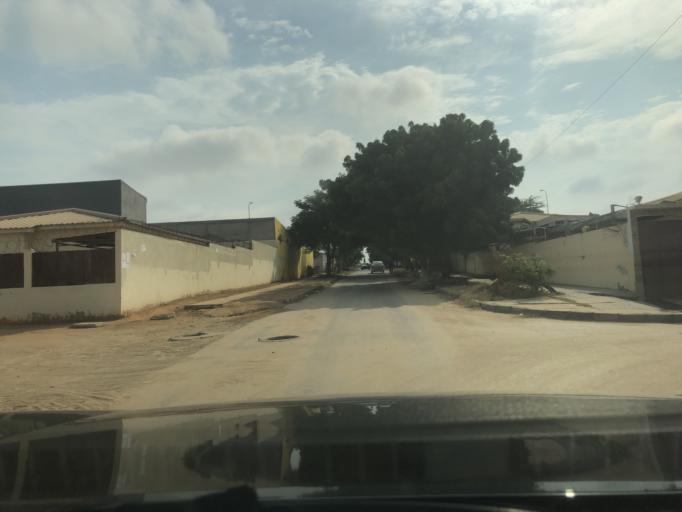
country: AO
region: Luanda
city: Luanda
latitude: -8.9368
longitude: 13.2457
